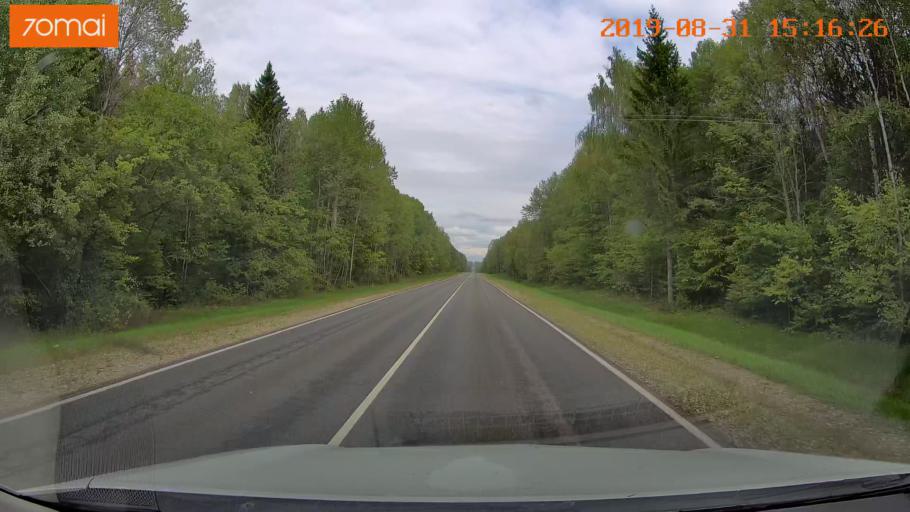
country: RU
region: Kaluga
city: Baryatino
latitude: 54.4599
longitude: 34.3503
